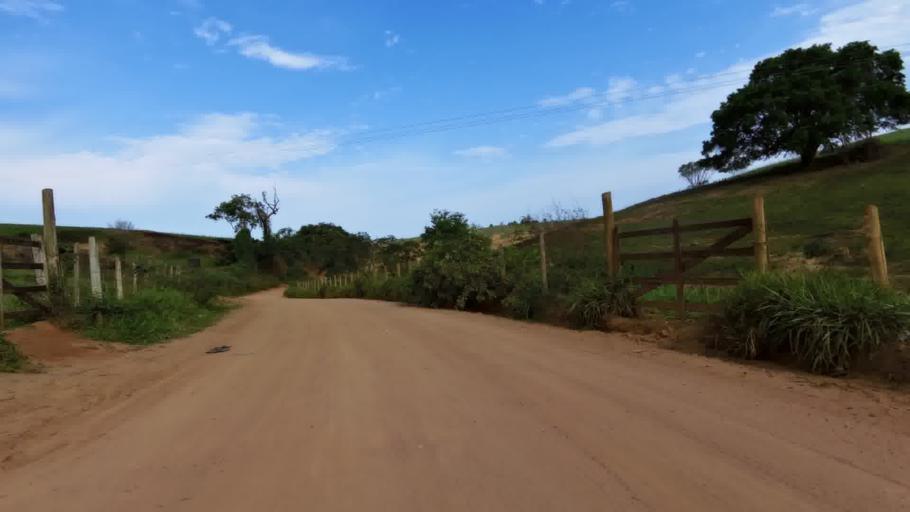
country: BR
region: Espirito Santo
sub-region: Piuma
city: Piuma
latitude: -20.8335
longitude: -40.7387
